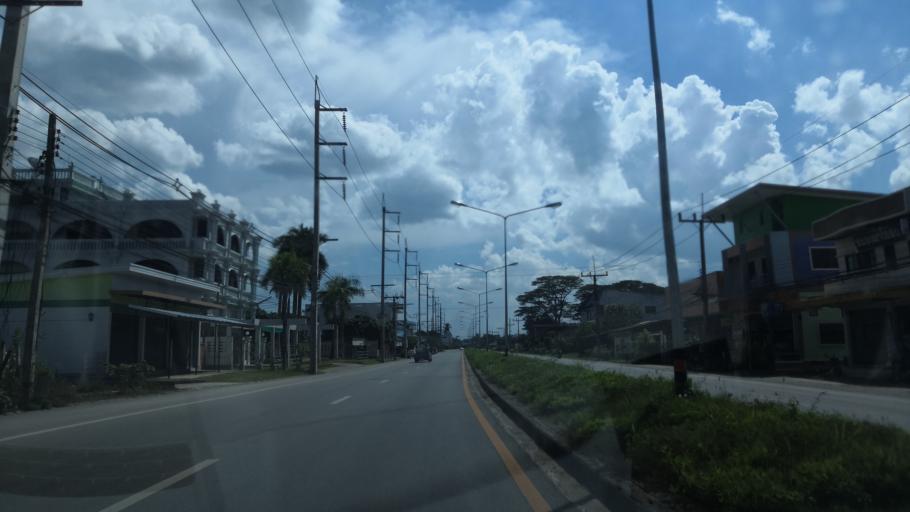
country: TH
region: Chiang Rai
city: Mae Suai
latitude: 19.5723
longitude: 99.4932
